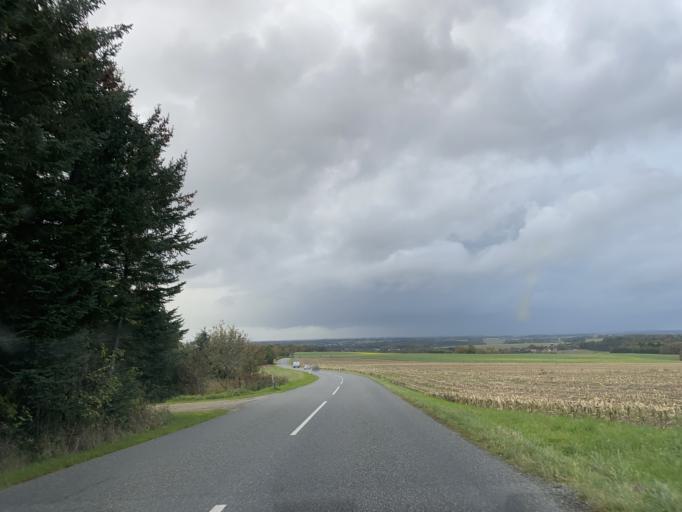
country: DK
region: Central Jutland
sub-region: Skanderborg Kommune
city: Ry
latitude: 56.2015
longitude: 9.7569
